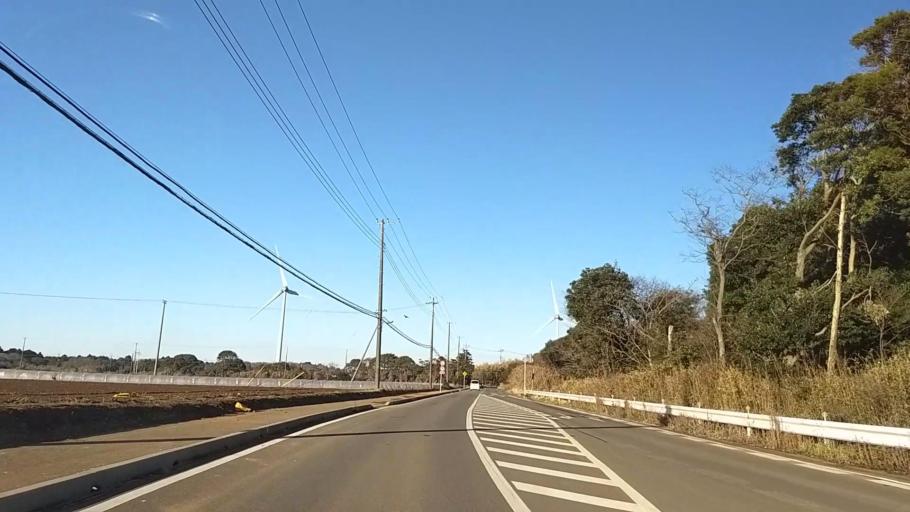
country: JP
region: Chiba
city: Hasaki
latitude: 35.7529
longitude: 140.7396
